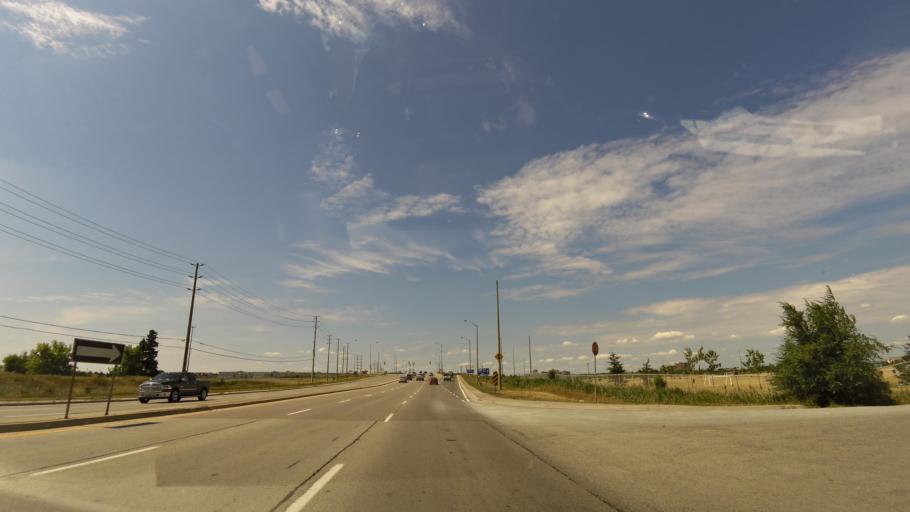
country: CA
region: Ontario
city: Brampton
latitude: 43.6848
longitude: -79.6872
